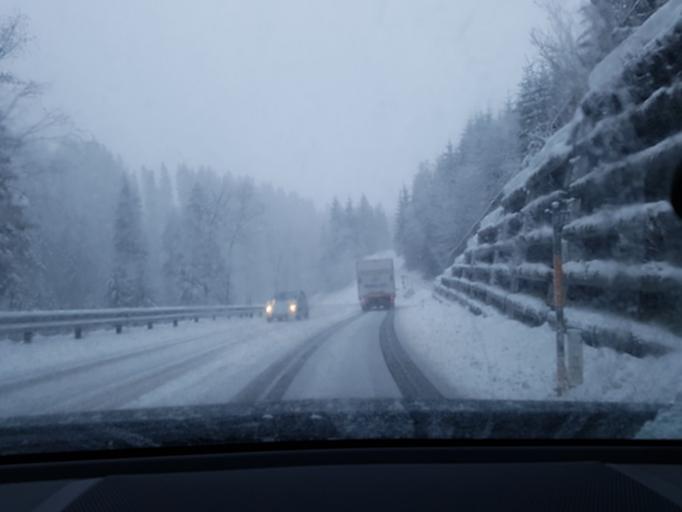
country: AT
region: Salzburg
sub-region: Politischer Bezirk Hallein
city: Abtenau
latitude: 47.5890
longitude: 13.3166
